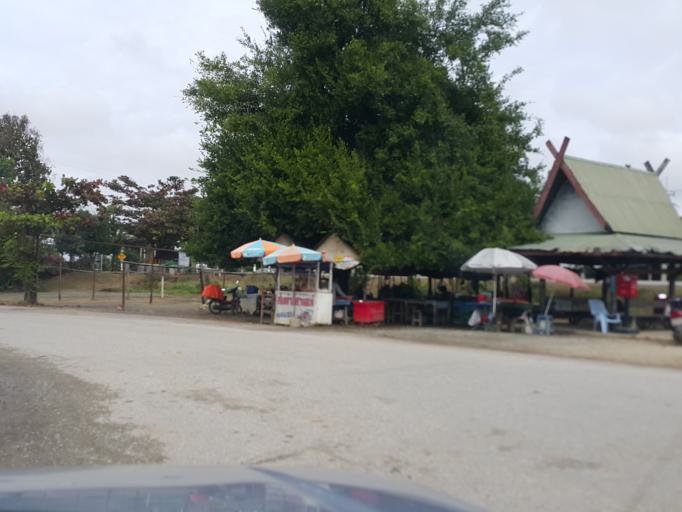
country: TH
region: Chiang Mai
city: San Kamphaeng
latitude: 18.7200
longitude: 99.1116
